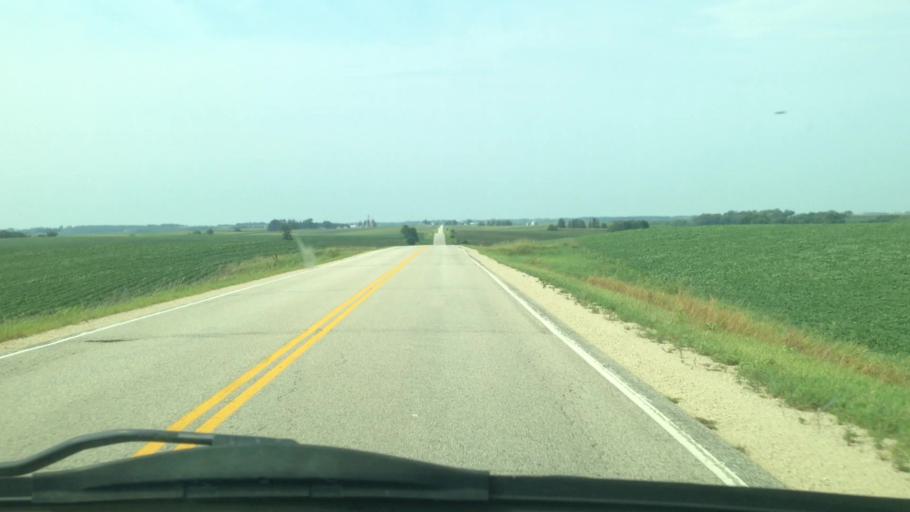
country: US
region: Minnesota
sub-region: Winona County
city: Saint Charles
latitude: 43.8619
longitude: -91.9593
